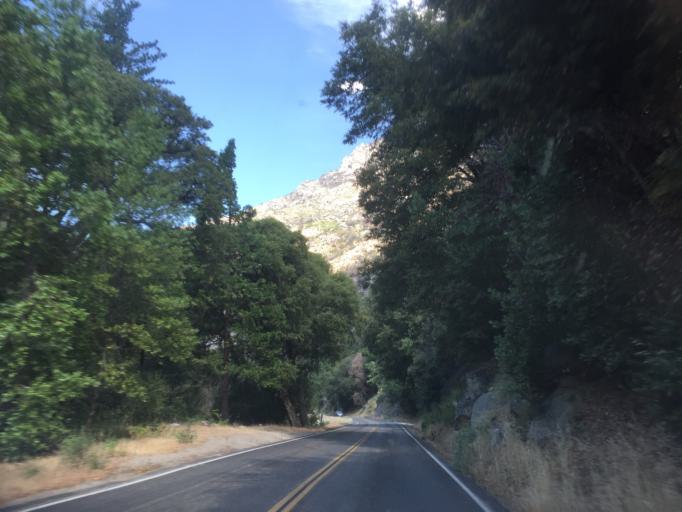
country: US
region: California
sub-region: Tulare County
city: Three Rivers
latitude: 36.8073
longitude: -118.7506
